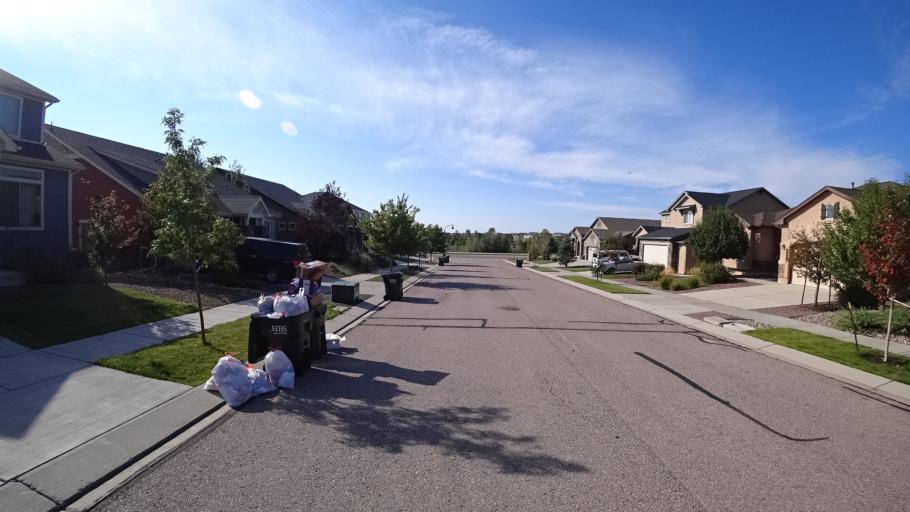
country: US
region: Colorado
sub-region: El Paso County
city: Cimarron Hills
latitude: 38.9354
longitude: -104.6725
